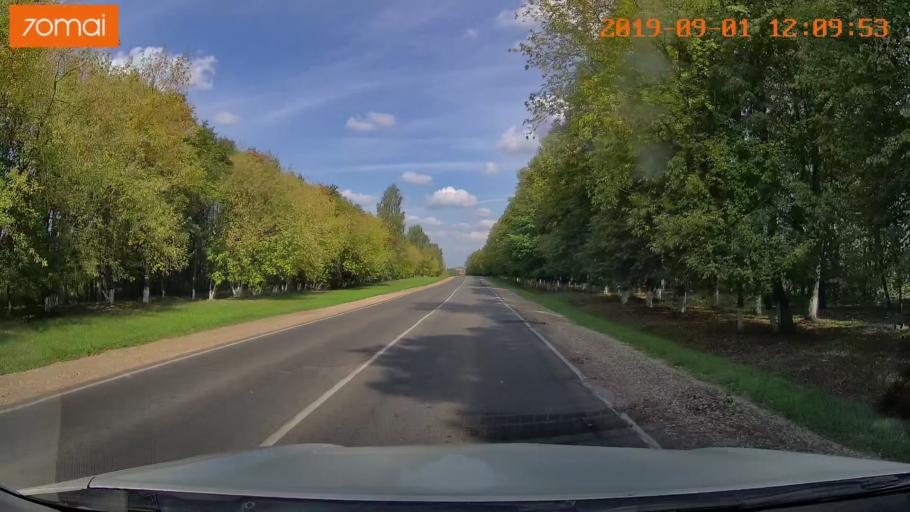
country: RU
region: Kaluga
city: Maloyaroslavets
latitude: 54.9854
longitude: 36.4291
